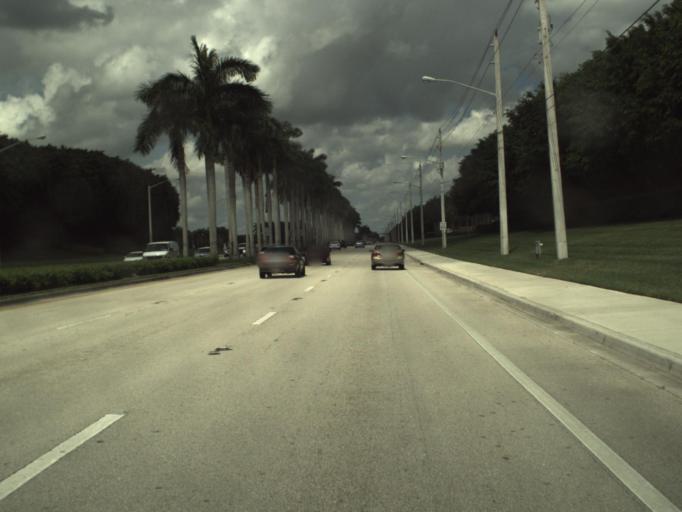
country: US
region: Florida
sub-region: Palm Beach County
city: Wellington
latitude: 26.6509
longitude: -80.1832
